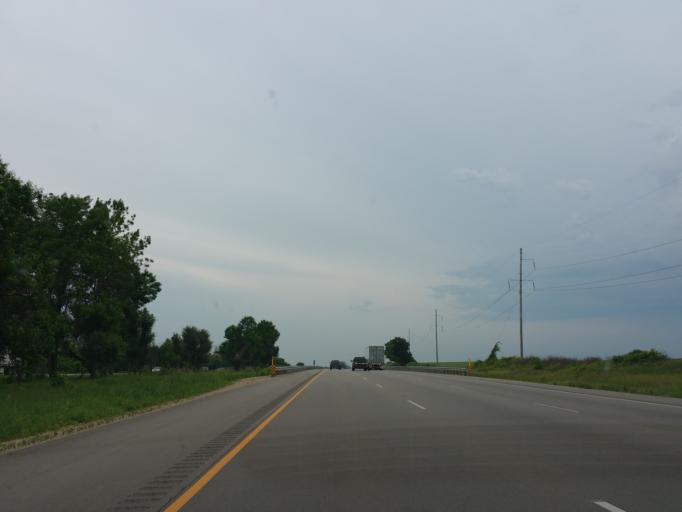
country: US
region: Wisconsin
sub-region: Dane County
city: De Forest
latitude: 43.2371
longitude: -89.3707
